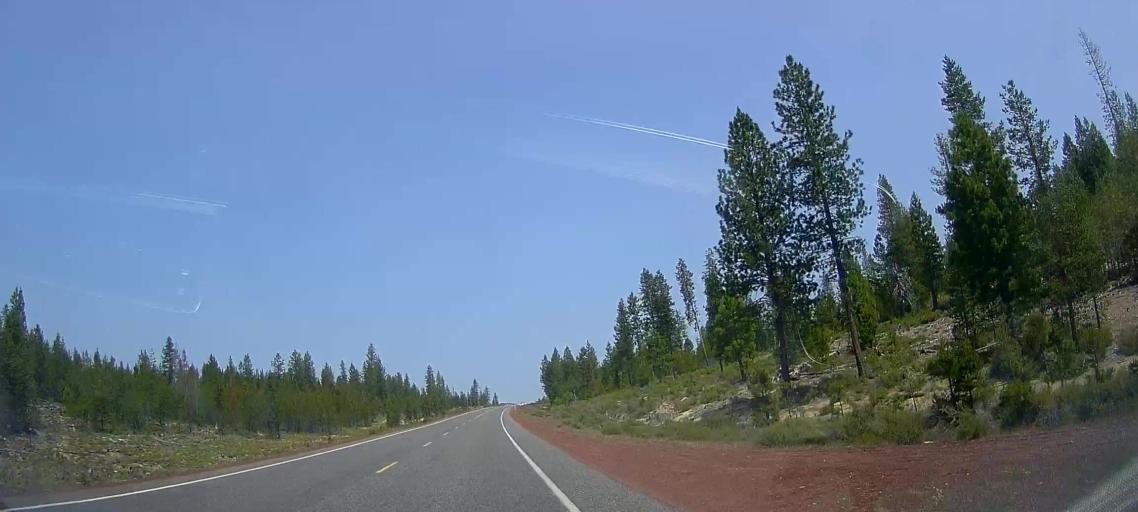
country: US
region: Oregon
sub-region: Deschutes County
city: La Pine
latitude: 43.4100
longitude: -121.7220
